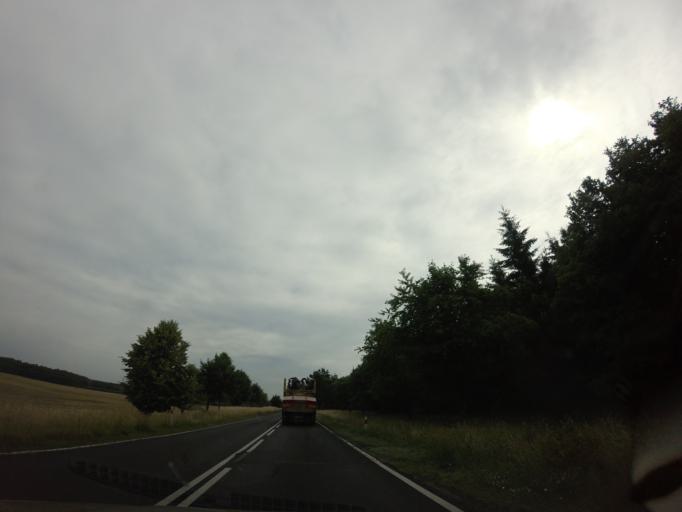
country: PL
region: West Pomeranian Voivodeship
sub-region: Powiat drawski
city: Kalisz Pomorski
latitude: 53.3066
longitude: 15.9848
